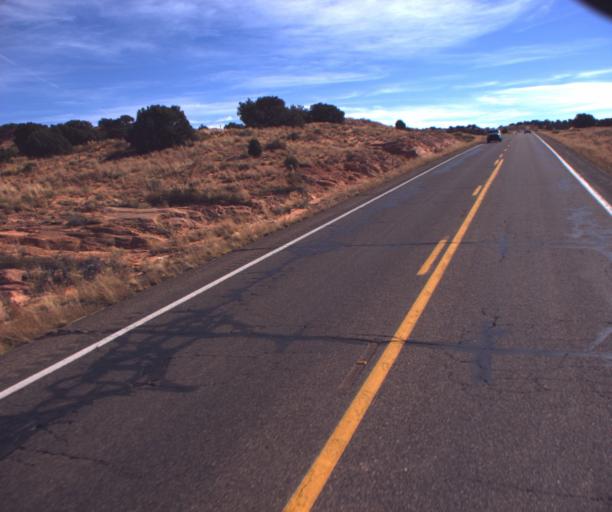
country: US
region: Arizona
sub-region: Coconino County
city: Kaibito
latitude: 36.5774
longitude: -111.1285
